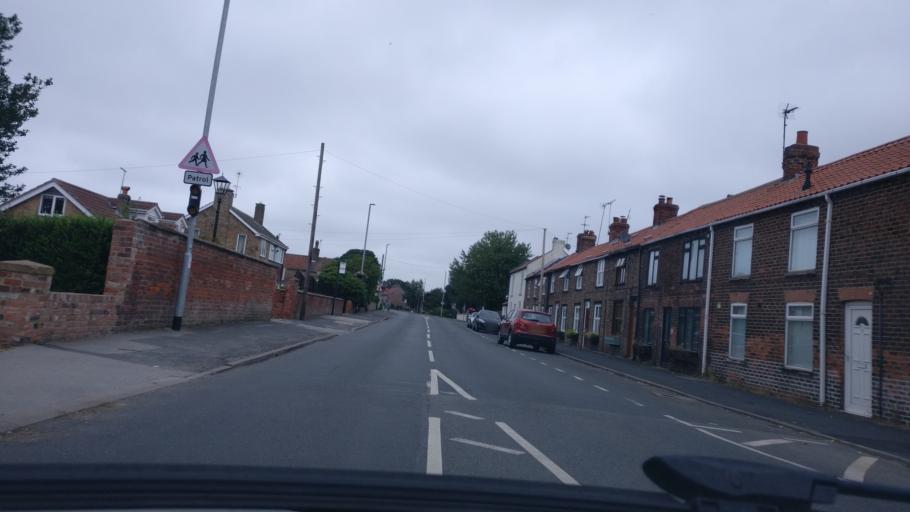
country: GB
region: England
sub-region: East Riding of Yorkshire
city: Leven
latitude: 53.8894
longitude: -0.3161
